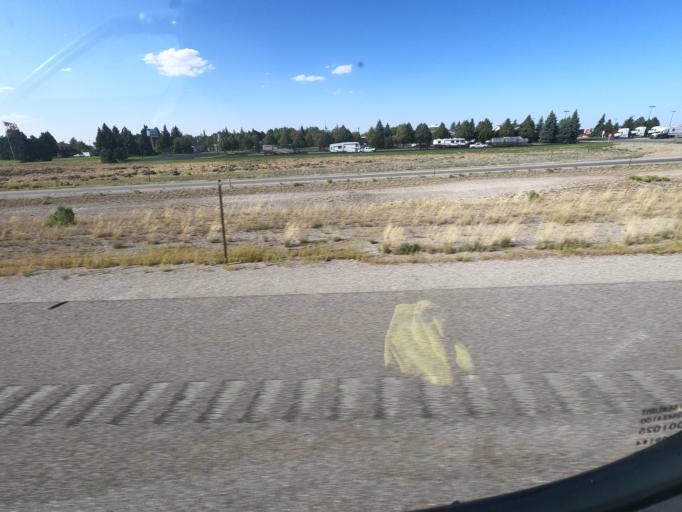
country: US
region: Wyoming
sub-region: Sweetwater County
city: Green River
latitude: 41.5425
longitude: -109.8589
